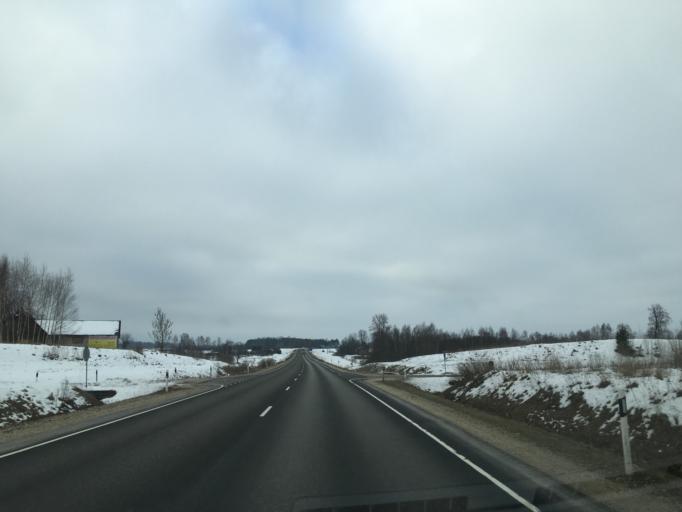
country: EE
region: Tartu
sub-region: Elva linn
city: Elva
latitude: 58.1962
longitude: 26.3525
